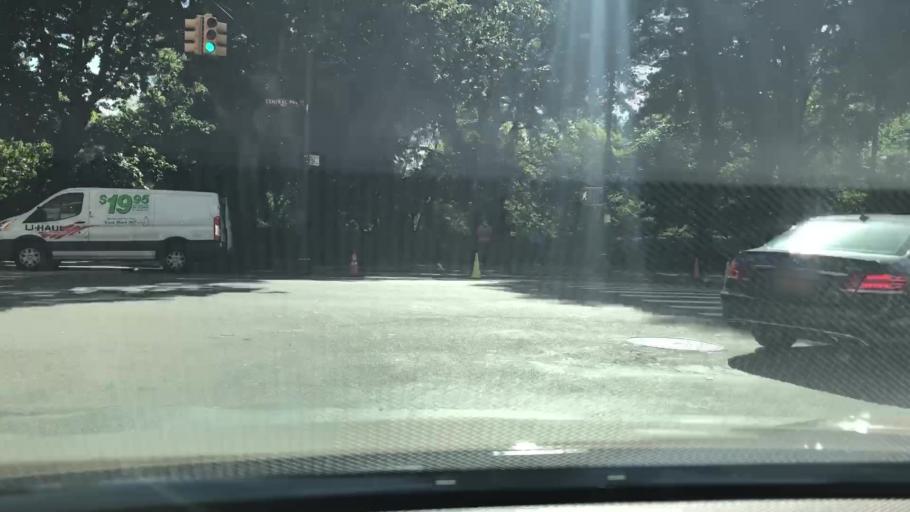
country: US
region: New York
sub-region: New York County
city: Manhattan
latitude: 40.7750
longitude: -73.9771
